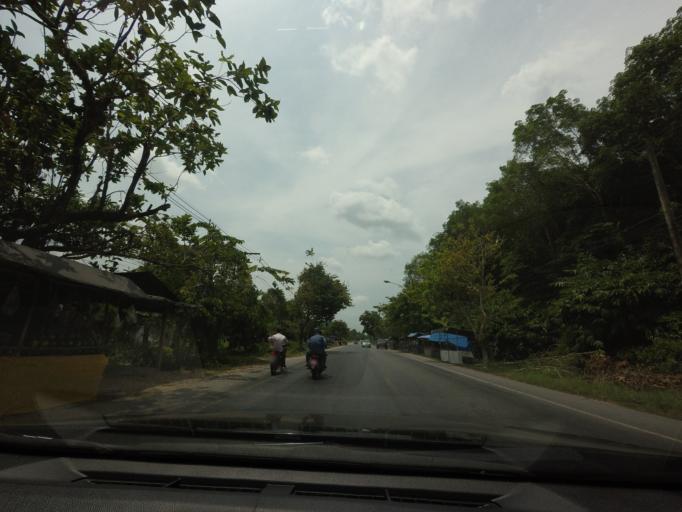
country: TH
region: Yala
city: Krong Pi Nang
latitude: 6.4646
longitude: 101.3287
